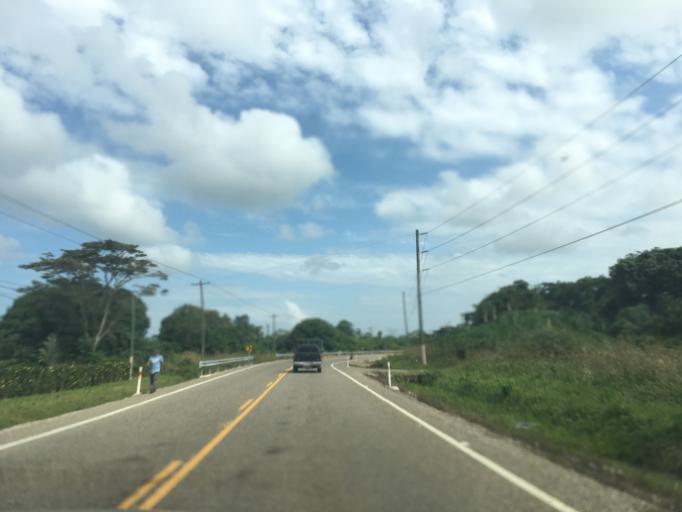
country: BZ
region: Stann Creek
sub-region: Dangriga
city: Dangriga
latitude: 17.0022
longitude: -88.3089
